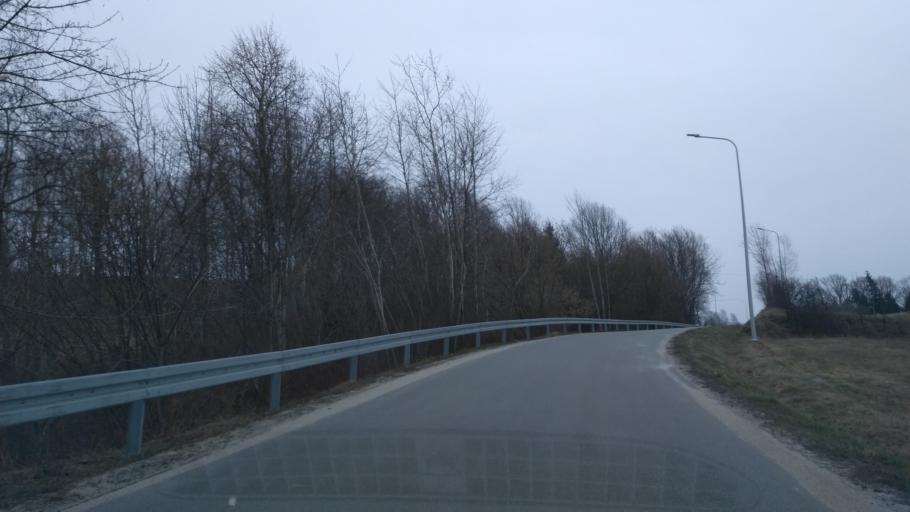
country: PL
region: Subcarpathian Voivodeship
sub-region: Powiat strzyzowski
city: Polomia
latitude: 49.9031
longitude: 21.8874
